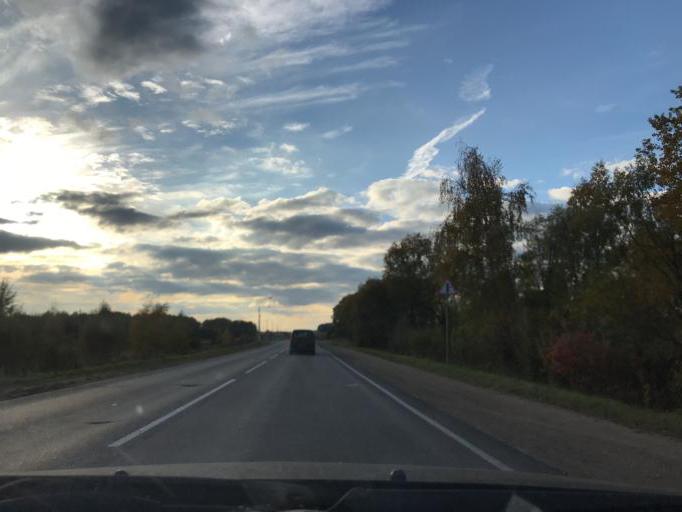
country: RU
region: Kaluga
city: Kurovskoye
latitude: 54.5291
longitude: 35.9616
